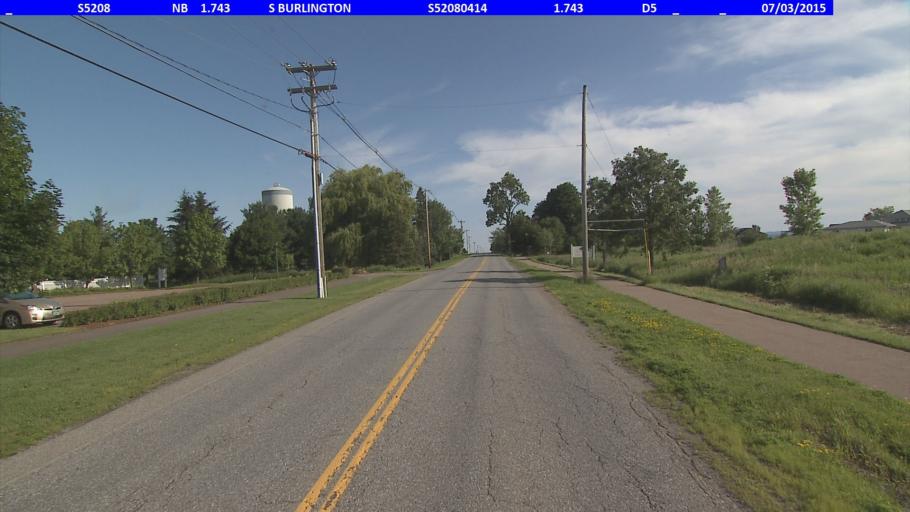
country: US
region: Vermont
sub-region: Chittenden County
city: South Burlington
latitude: 44.4357
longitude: -73.1758
